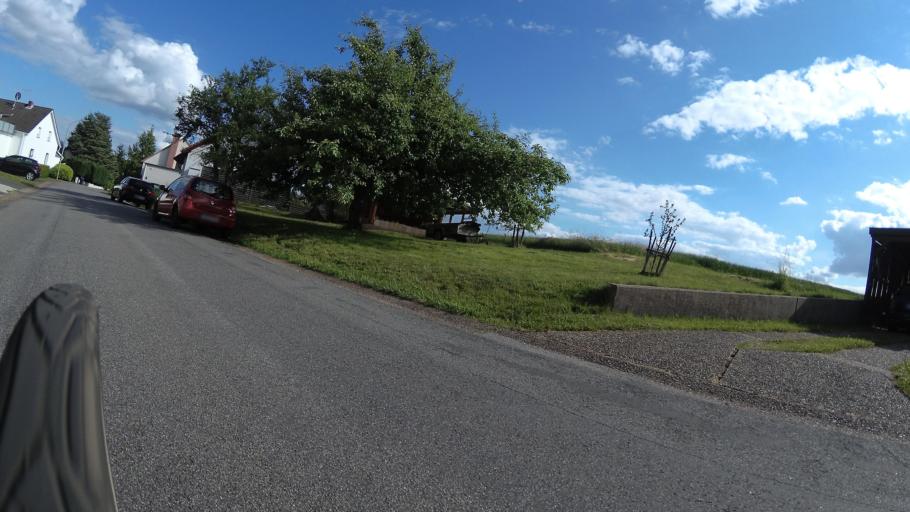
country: DE
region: Saarland
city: Heusweiler
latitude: 49.3430
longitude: 6.9578
